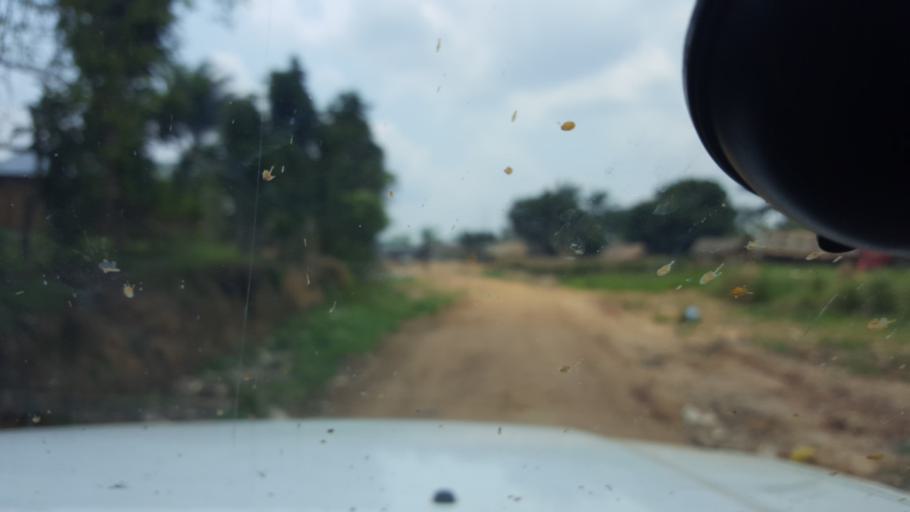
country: CD
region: Bandundu
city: Mushie
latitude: -3.7442
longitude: 16.6514
